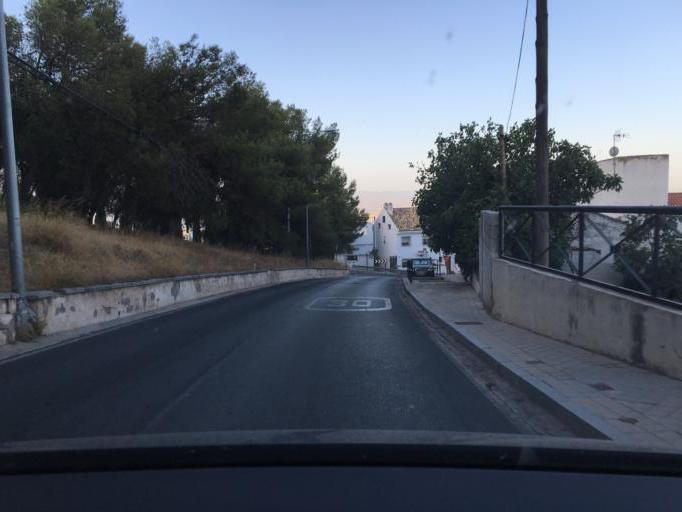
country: ES
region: Andalusia
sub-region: Provincia de Granada
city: Granada
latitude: 37.1903
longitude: -3.5885
